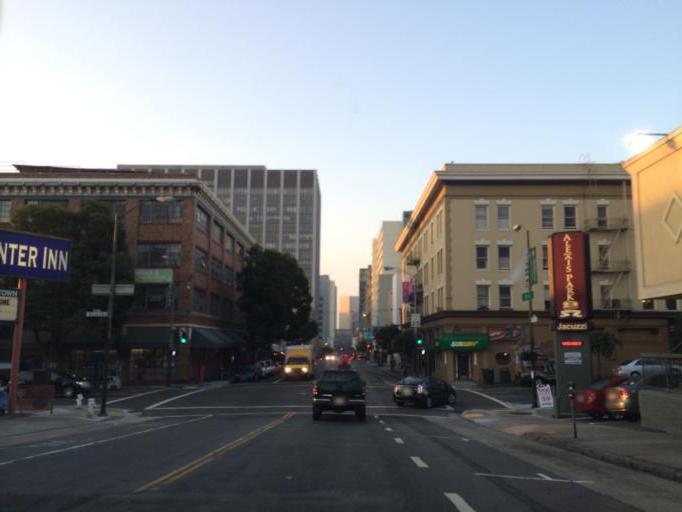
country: US
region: California
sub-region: San Francisco County
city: San Francisco
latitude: 37.7844
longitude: -122.4195
